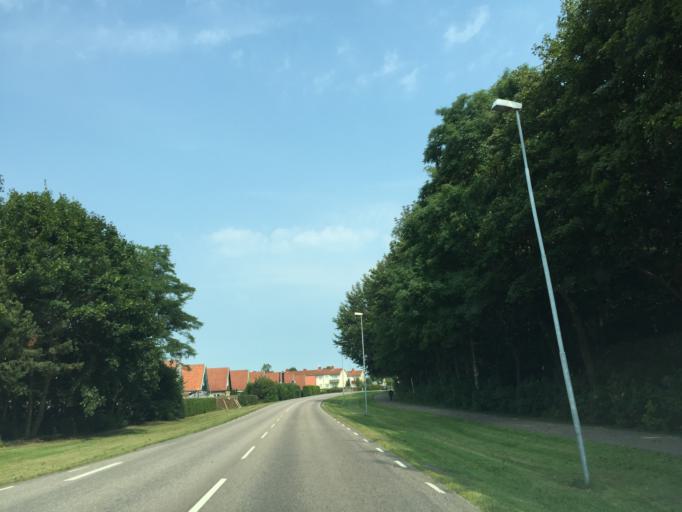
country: SE
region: Skane
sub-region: Angelholms Kommun
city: AEngelholm
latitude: 56.2330
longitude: 12.8490
